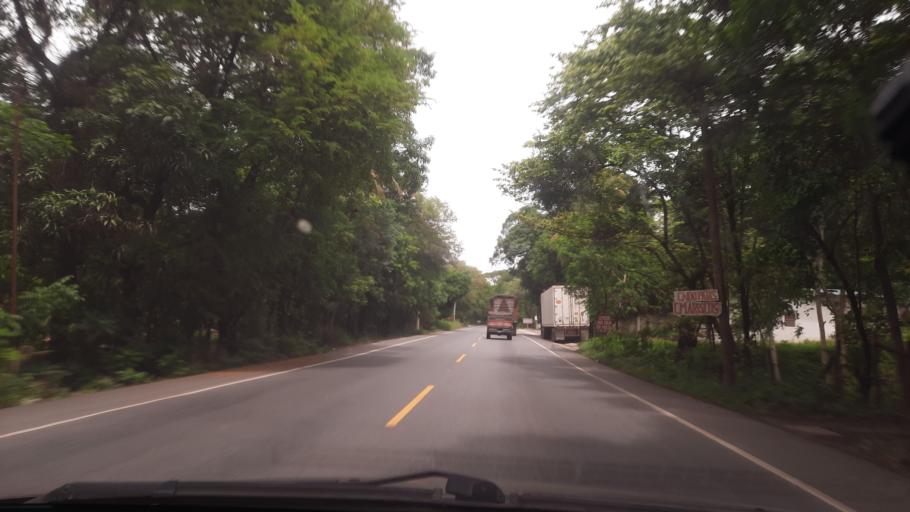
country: GT
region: Zacapa
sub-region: Municipio de Zacapa
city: Gualan
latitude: 15.1939
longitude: -89.2783
